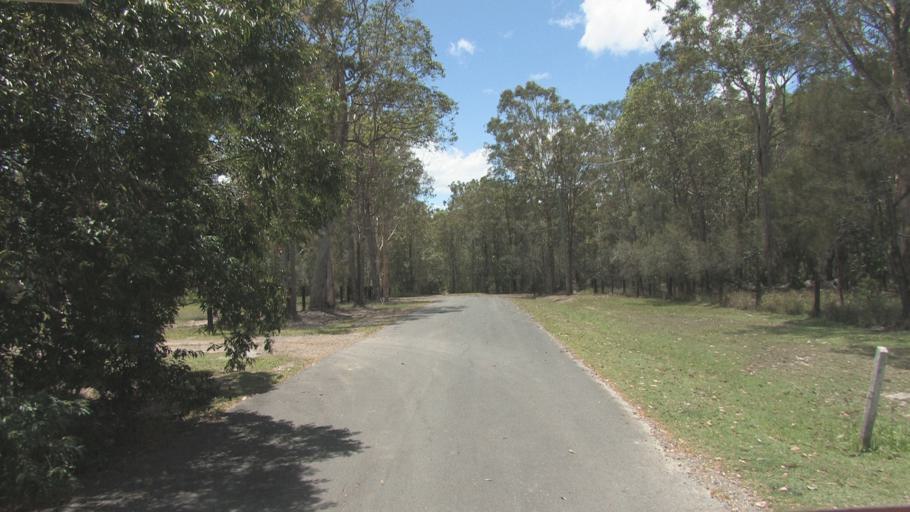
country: AU
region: Queensland
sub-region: Redland
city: Redland Bay
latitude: -27.6695
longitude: 153.2781
